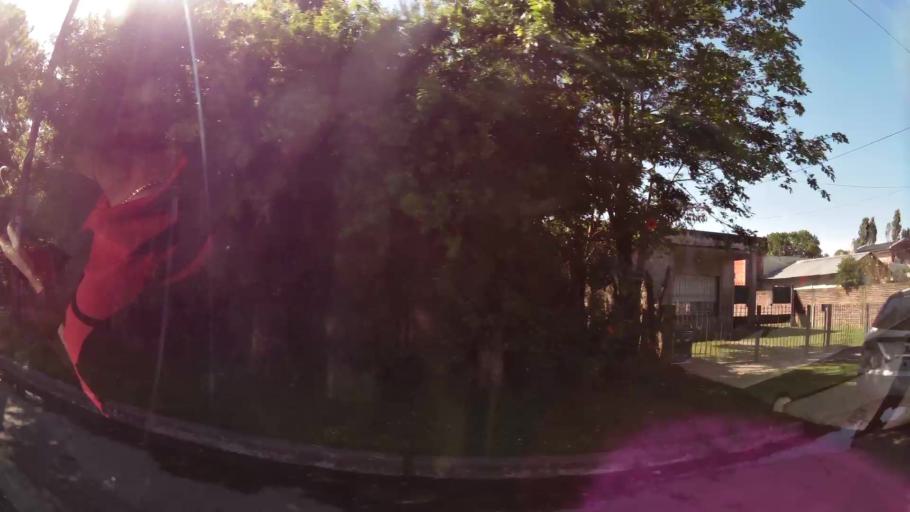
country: AR
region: Buenos Aires
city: Hurlingham
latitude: -34.4937
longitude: -58.6943
